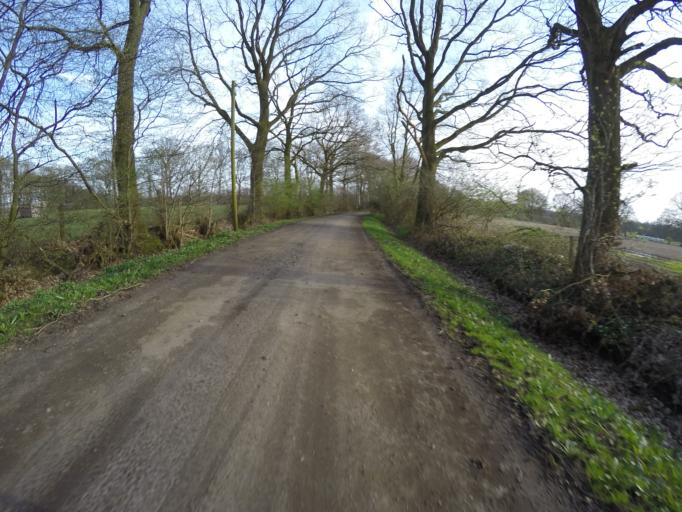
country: DE
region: Schleswig-Holstein
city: Hemdingen
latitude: 53.7284
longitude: 9.8354
